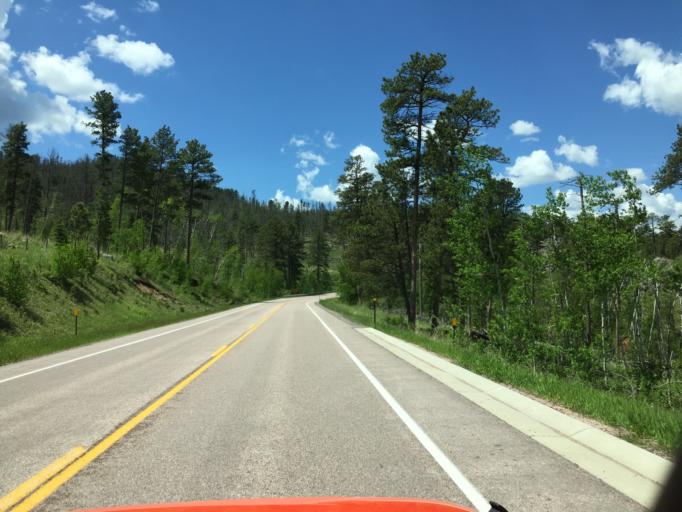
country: US
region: South Dakota
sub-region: Custer County
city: Custer
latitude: 43.8961
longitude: -103.5122
